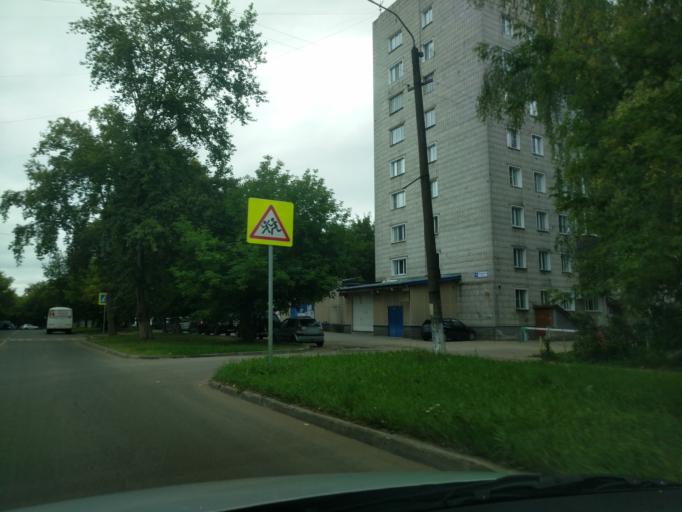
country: RU
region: Kirov
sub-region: Kirovo-Chepetskiy Rayon
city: Kirov
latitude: 58.6344
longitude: 49.6172
